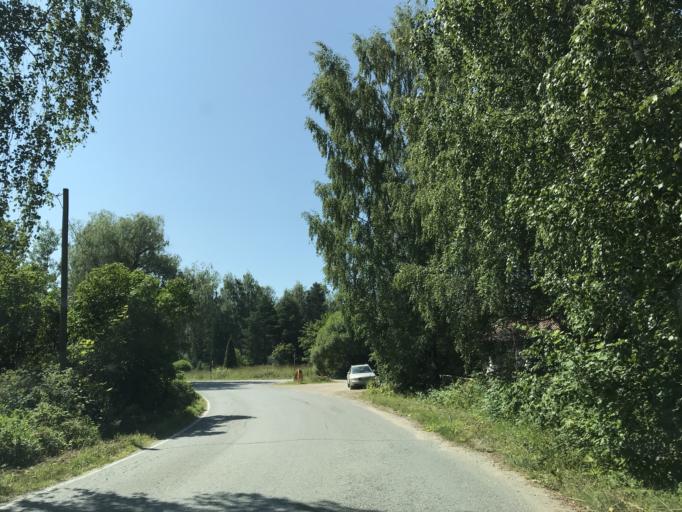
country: FI
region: Paijanne Tavastia
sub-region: Lahti
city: Asikkala
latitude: 61.1924
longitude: 25.6125
